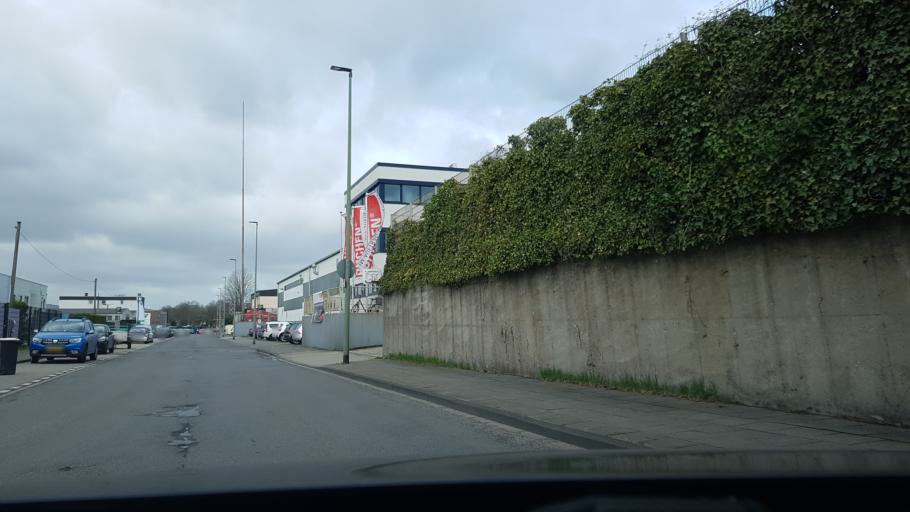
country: DE
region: North Rhine-Westphalia
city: Meiderich
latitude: 51.4903
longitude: 6.8010
